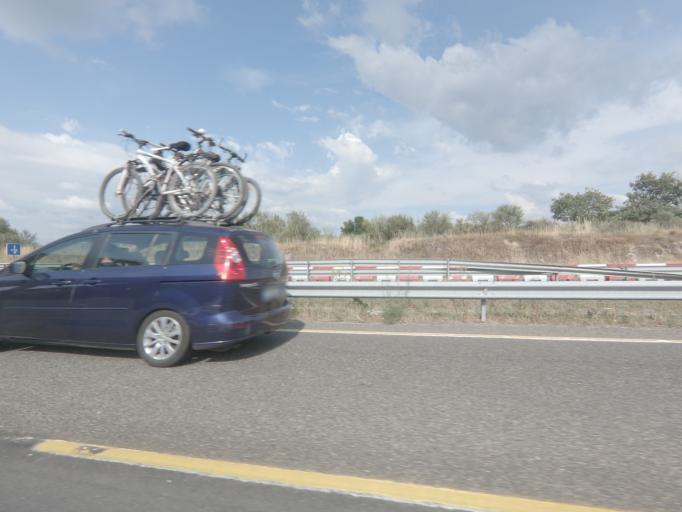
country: ES
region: Galicia
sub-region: Provincia de Ourense
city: Taboadela
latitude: 42.2420
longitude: -7.8594
